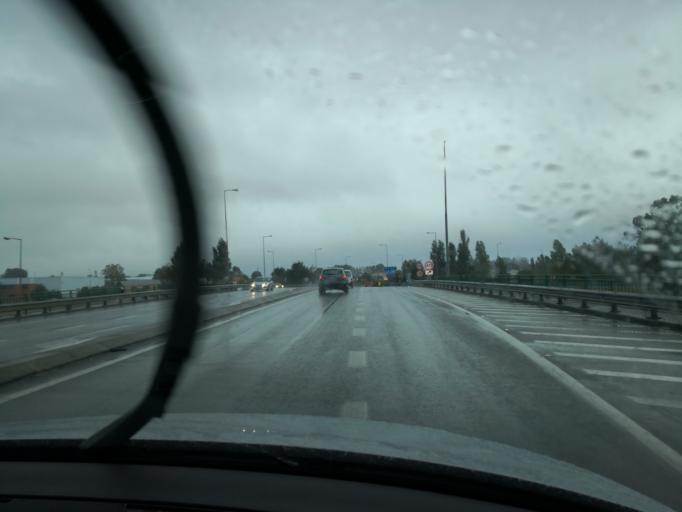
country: PT
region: Setubal
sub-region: Moita
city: Moita
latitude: 38.6441
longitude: -8.9753
